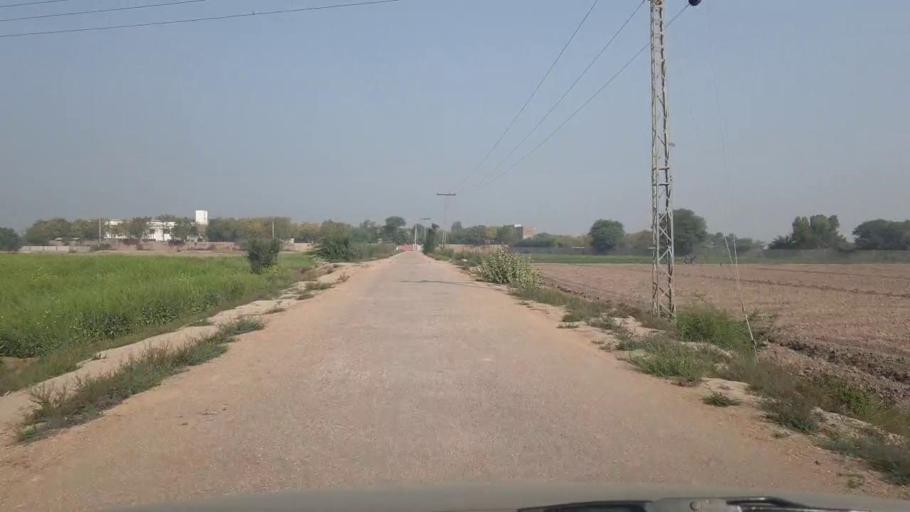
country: PK
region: Sindh
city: Umarkot
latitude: 25.3742
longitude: 69.7381
